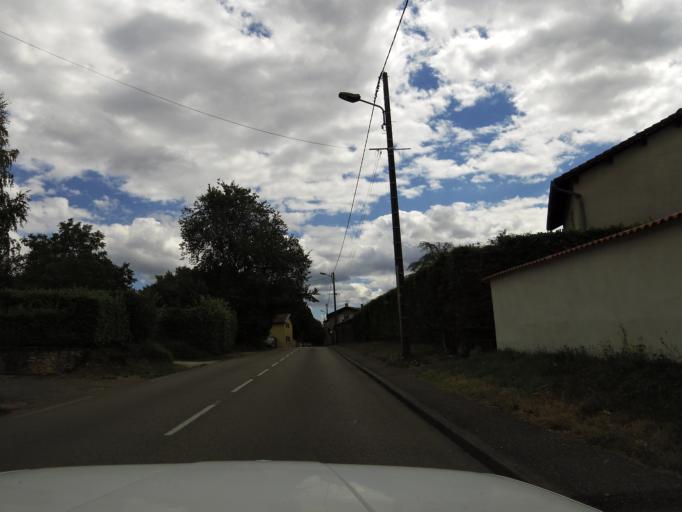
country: FR
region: Rhone-Alpes
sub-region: Departement de l'Ain
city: Chazey-sur-Ain
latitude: 45.8735
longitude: 5.2220
